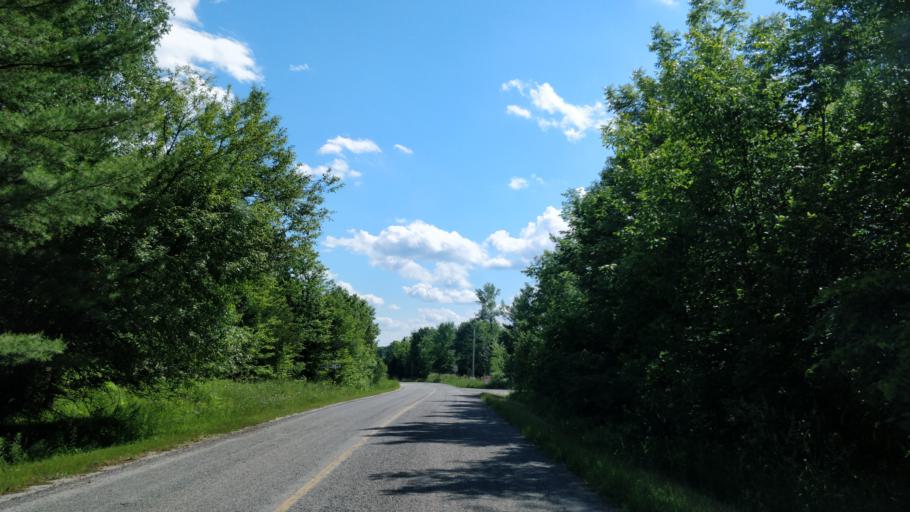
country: CA
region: Ontario
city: Perth
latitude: 44.7333
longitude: -76.5056
